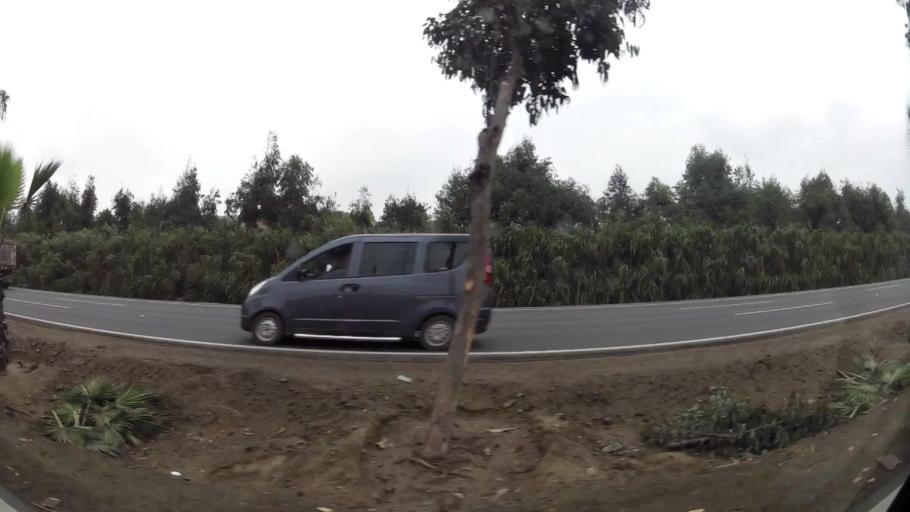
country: PE
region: Lima
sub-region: Lima
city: Punta Hermosa
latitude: -12.2680
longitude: -76.9027
